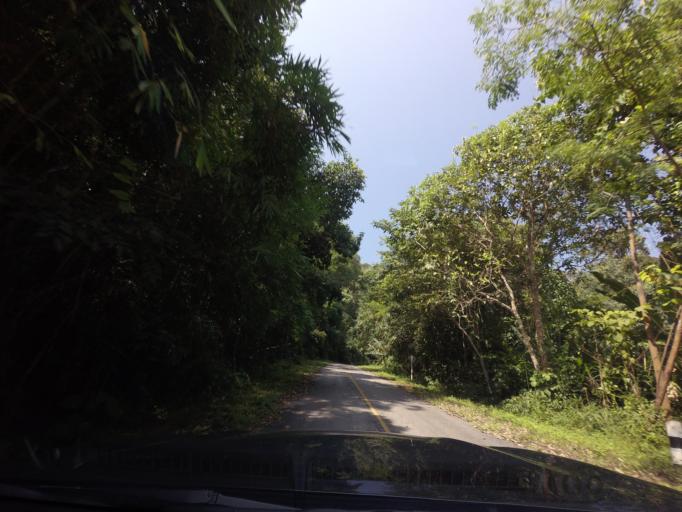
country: TH
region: Loei
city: Na Haeo
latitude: 17.5698
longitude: 100.9659
